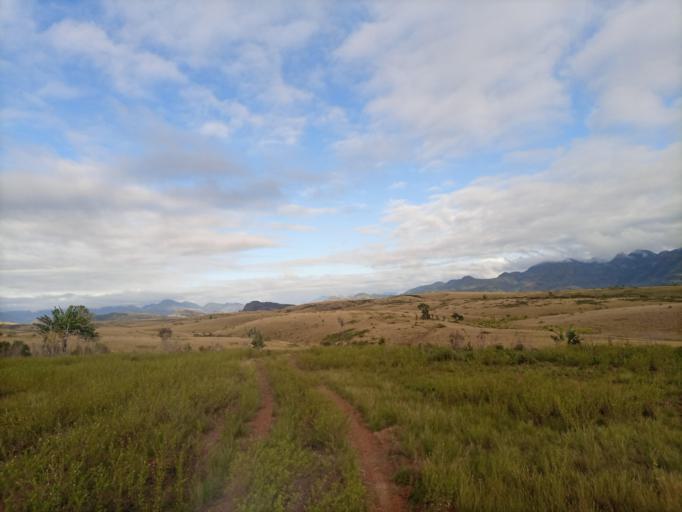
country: MG
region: Anosy
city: Fort Dauphin
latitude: -24.3092
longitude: 47.2463
